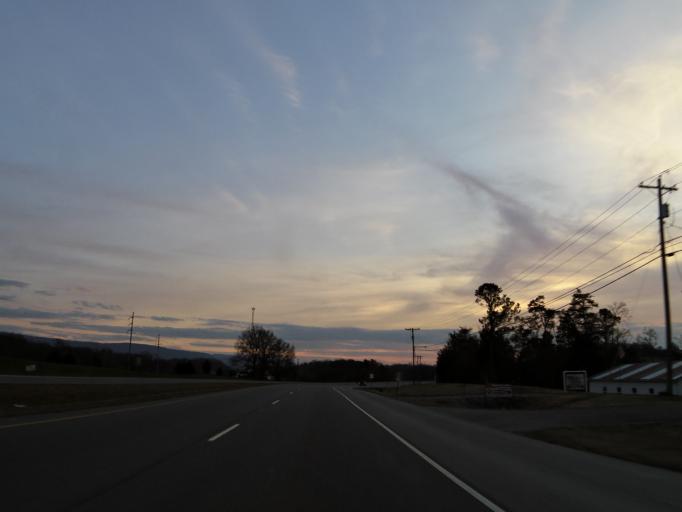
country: US
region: Tennessee
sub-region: McMinn County
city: Etowah
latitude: 35.3624
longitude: -84.5147
